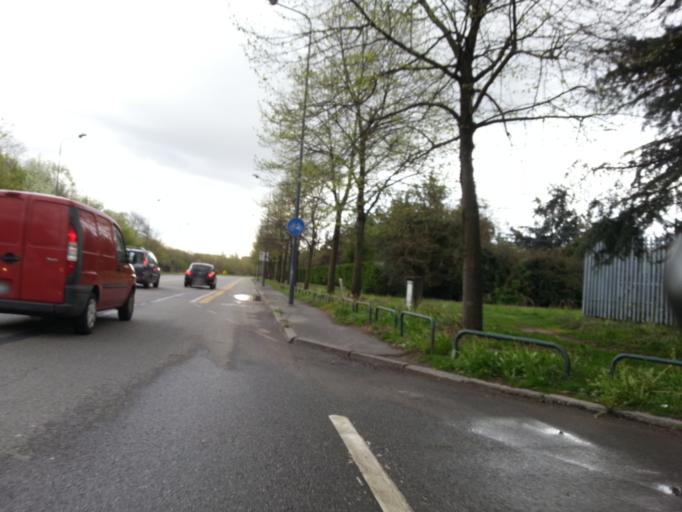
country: IT
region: Lombardy
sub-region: Citta metropolitana di Milano
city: Bresso
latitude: 45.5263
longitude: 9.1943
